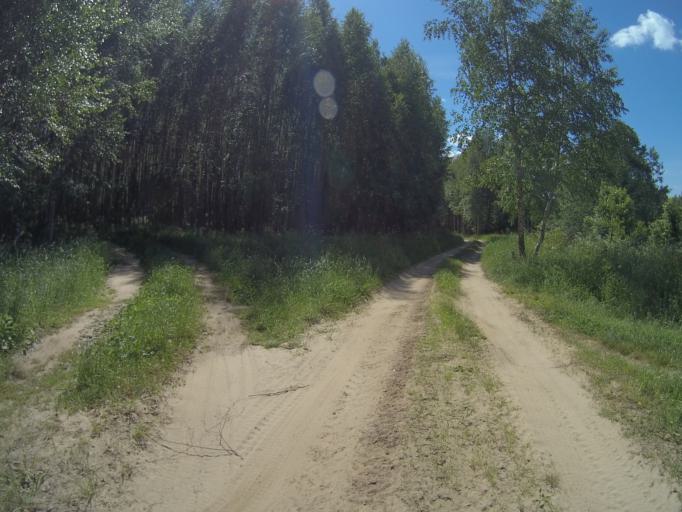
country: RU
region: Vladimir
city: Golovino
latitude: 56.0021
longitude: 40.4320
